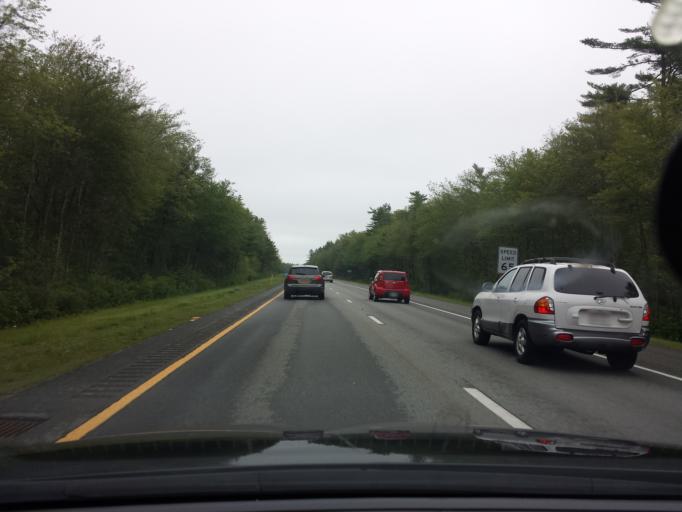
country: US
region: Massachusetts
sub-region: Plymouth County
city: Mattapoisett Center
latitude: 41.6966
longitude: -70.8011
